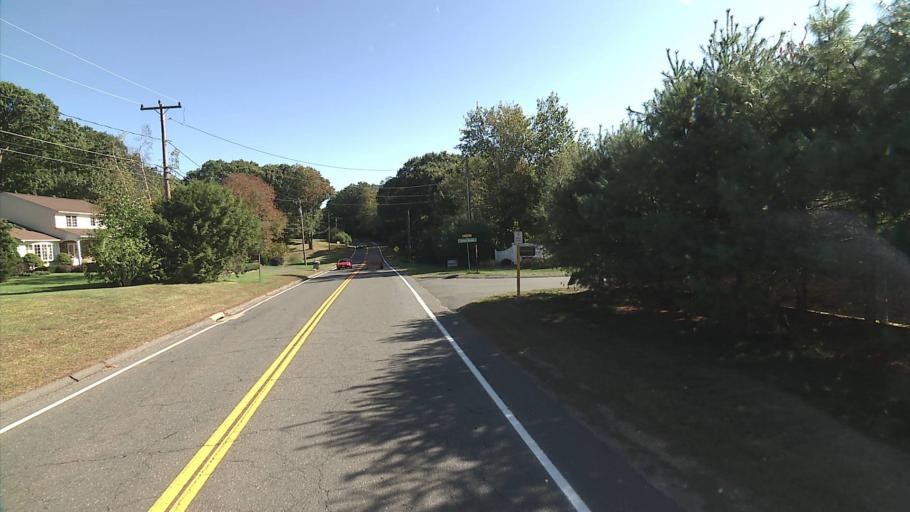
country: US
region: Connecticut
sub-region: Hartford County
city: Collinsville
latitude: 41.7633
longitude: -72.9736
